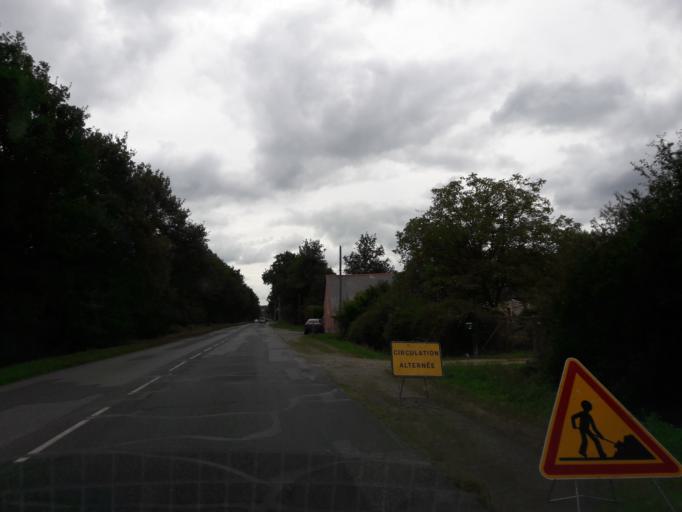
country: FR
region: Brittany
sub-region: Departement d'Ille-et-Vilaine
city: Orgeres
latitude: 48.0026
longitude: -1.6969
